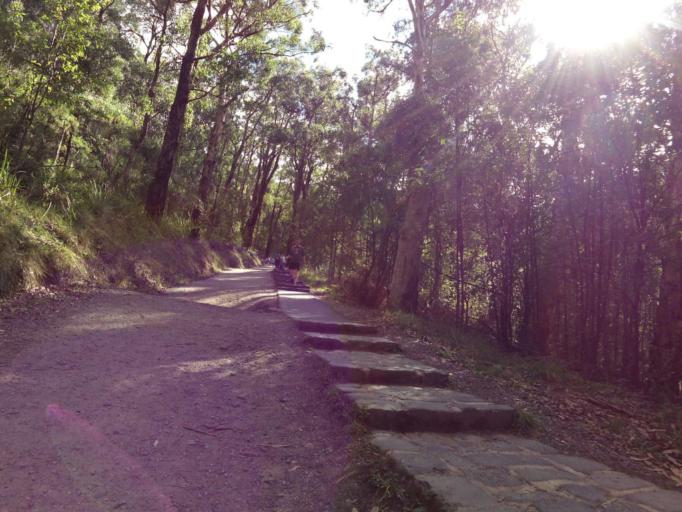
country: AU
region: Victoria
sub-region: Yarra Ranges
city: Ferny Creek
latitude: -37.8863
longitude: 145.3171
